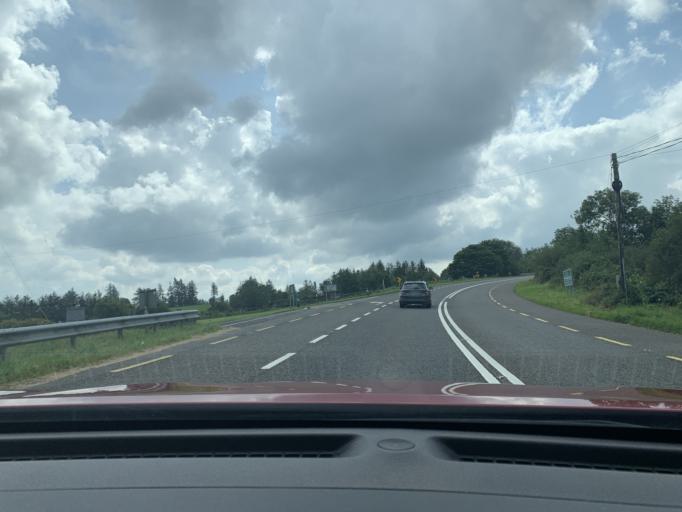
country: IE
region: Connaught
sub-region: Sligo
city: Tobercurry
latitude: 53.9270
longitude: -8.7839
